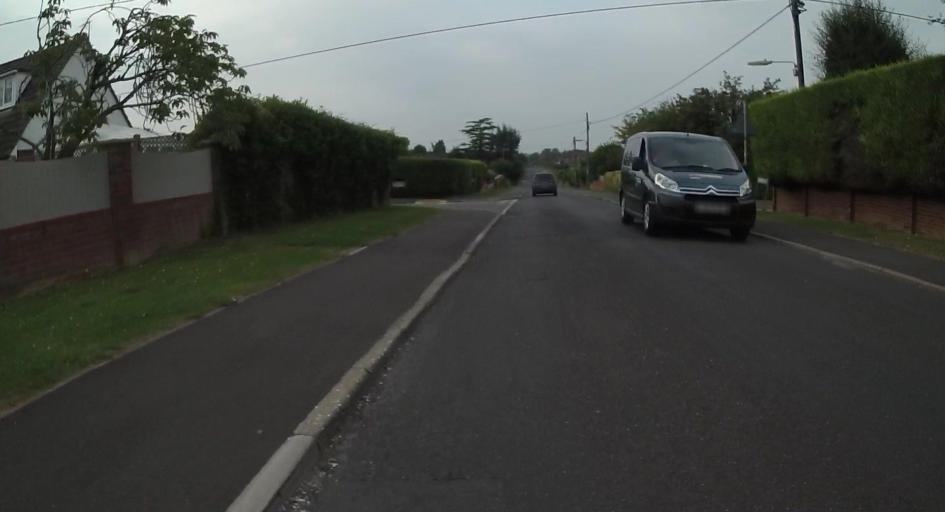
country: GB
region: England
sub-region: Hampshire
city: Old Basing
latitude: 51.2642
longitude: -1.0426
